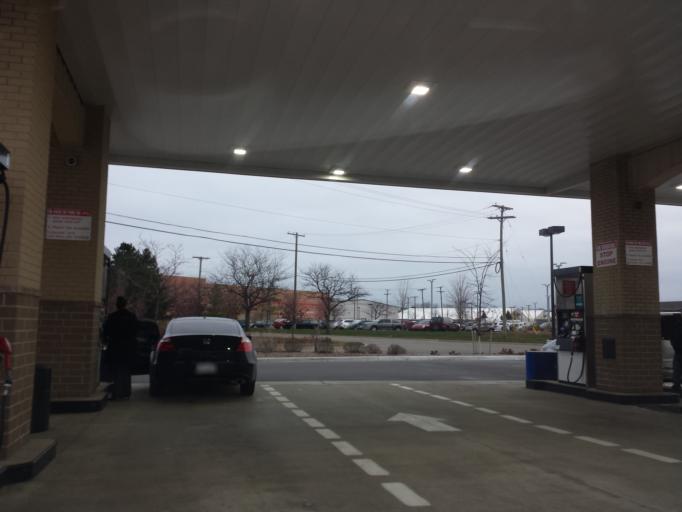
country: US
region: Michigan
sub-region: Oakland County
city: Pontiac
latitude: 42.6054
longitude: -83.2937
